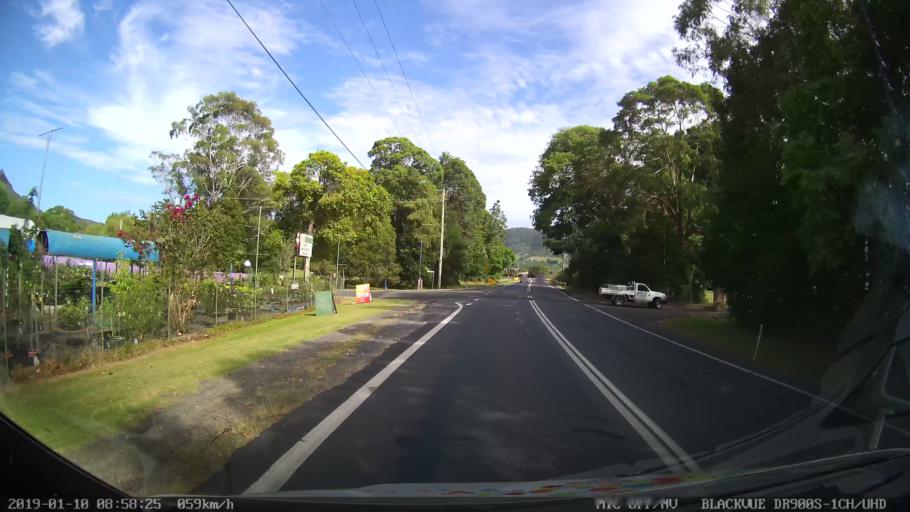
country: AU
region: New South Wales
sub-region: Coffs Harbour
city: Coffs Harbour
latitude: -30.2897
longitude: 153.0878
